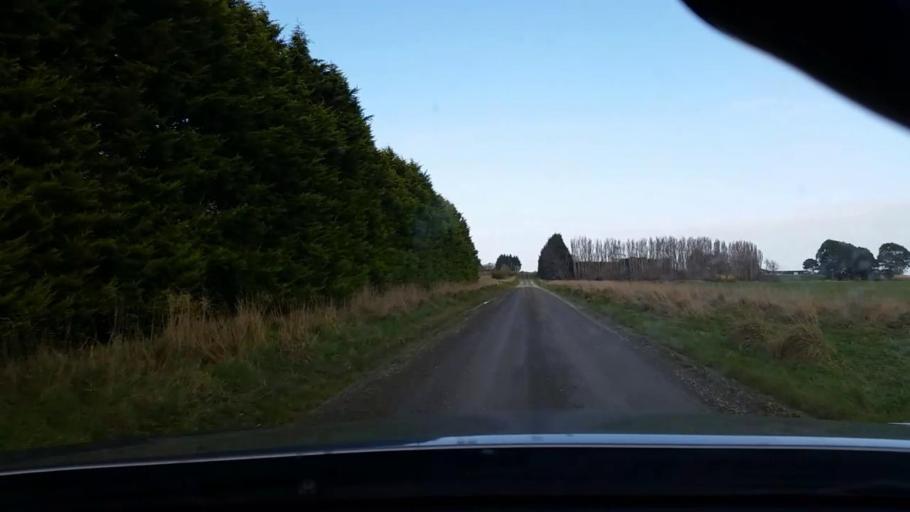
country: NZ
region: Southland
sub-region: Southland District
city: Winton
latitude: -46.2744
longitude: 168.2923
